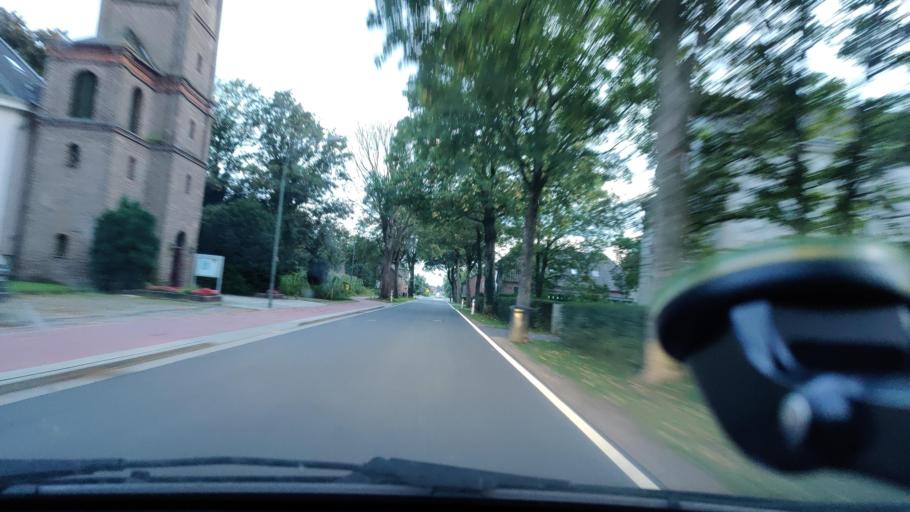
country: DE
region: North Rhine-Westphalia
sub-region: Regierungsbezirk Dusseldorf
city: Goch
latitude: 51.7187
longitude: 6.1892
